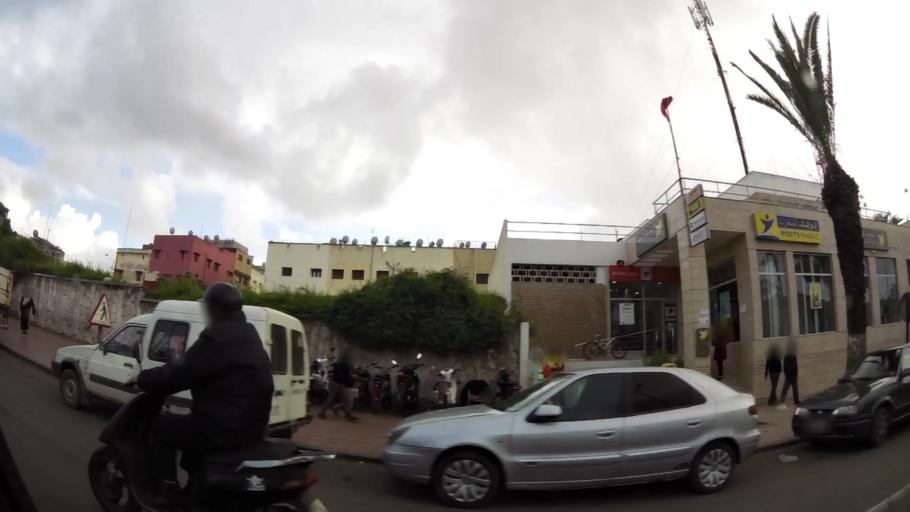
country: MA
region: Grand Casablanca
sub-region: Mohammedia
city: Mohammedia
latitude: 33.6870
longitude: -7.3905
